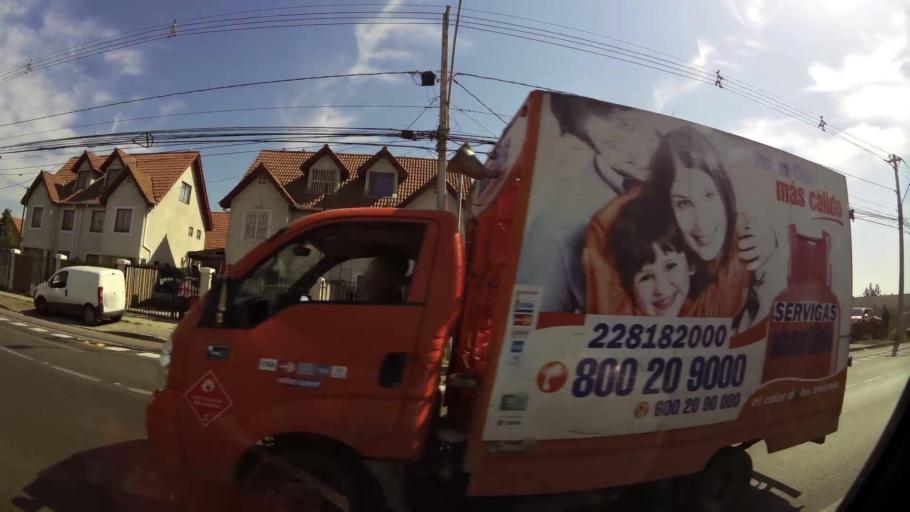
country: CL
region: Santiago Metropolitan
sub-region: Provincia de Talagante
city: Talagante
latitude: -33.6709
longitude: -70.9422
